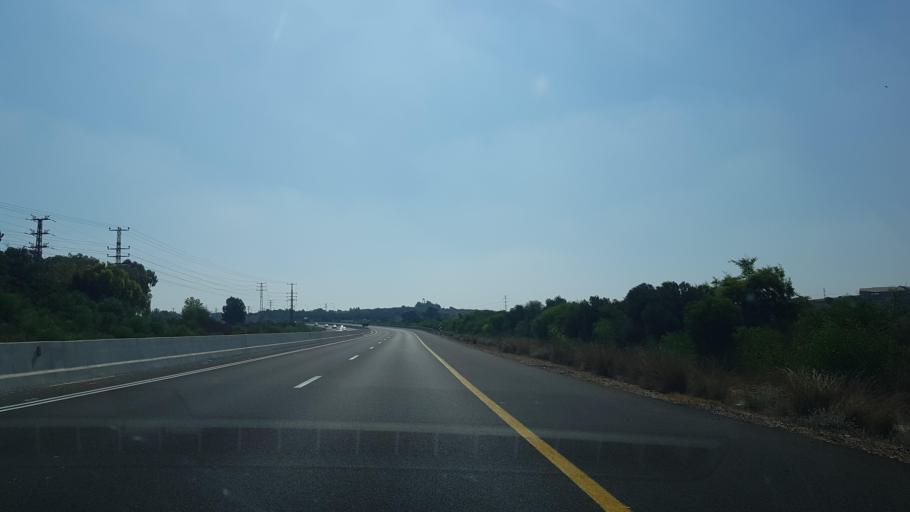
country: IL
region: Southern District
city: Ashqelon
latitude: 31.6887
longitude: 34.6706
